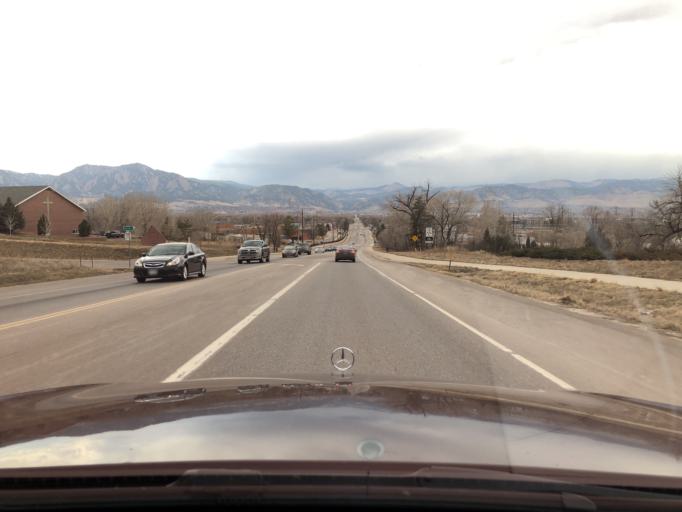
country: US
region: Colorado
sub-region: Boulder County
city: Gunbarrel
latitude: 40.0146
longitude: -105.1934
